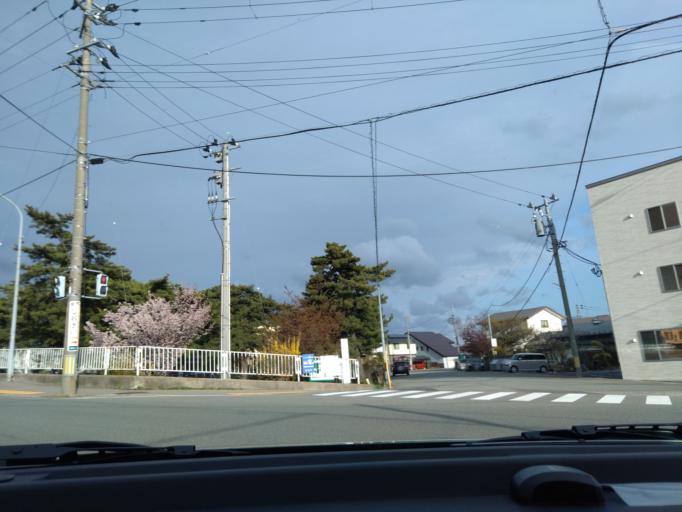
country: JP
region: Akita
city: Akita Shi
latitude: 39.7555
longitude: 140.0748
